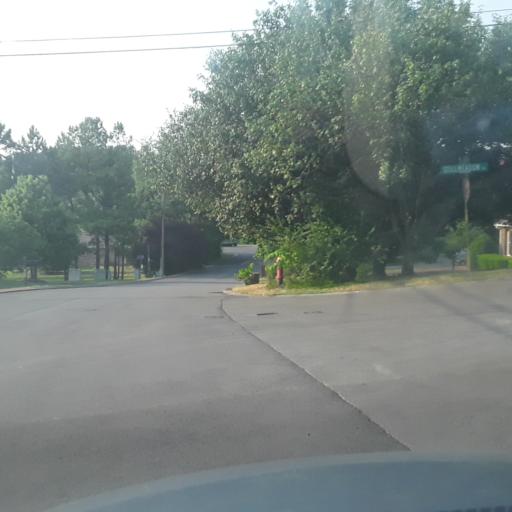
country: US
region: Tennessee
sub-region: Williamson County
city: Brentwood Estates
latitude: 36.0380
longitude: -86.7378
